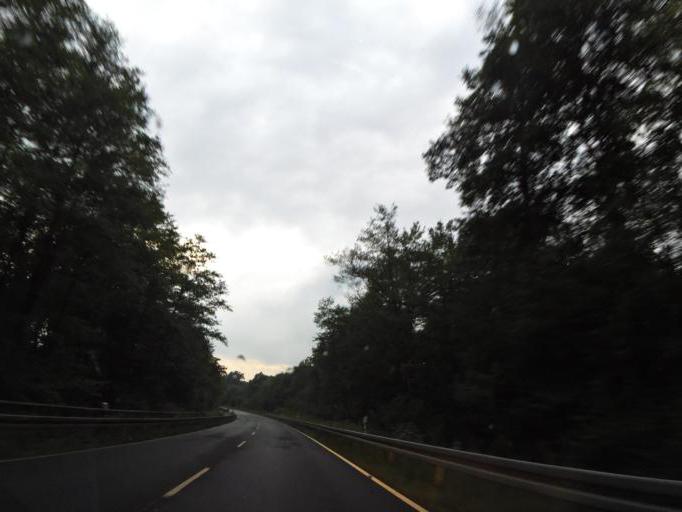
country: DE
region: Hesse
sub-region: Regierungsbezirk Darmstadt
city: Messel
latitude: 49.9104
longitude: 8.7700
